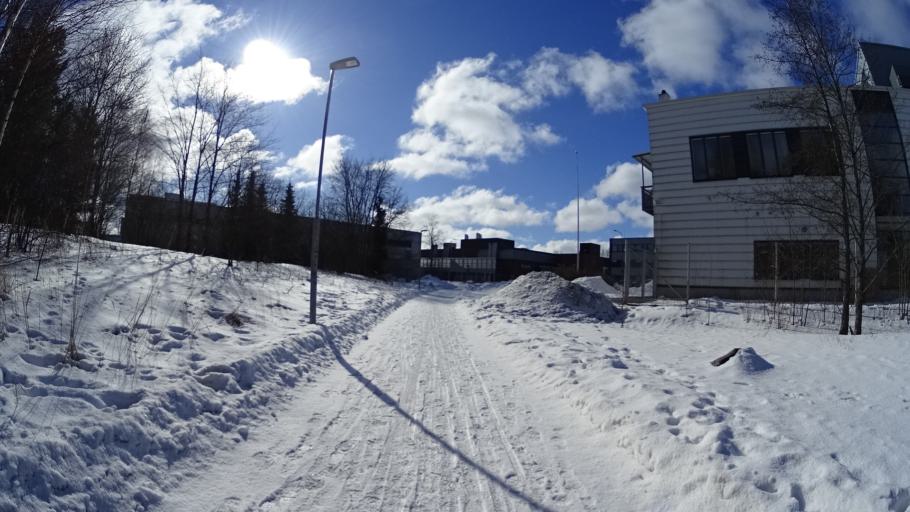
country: FI
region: Uusimaa
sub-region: Helsinki
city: Teekkarikylae
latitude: 60.2398
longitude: 24.8577
